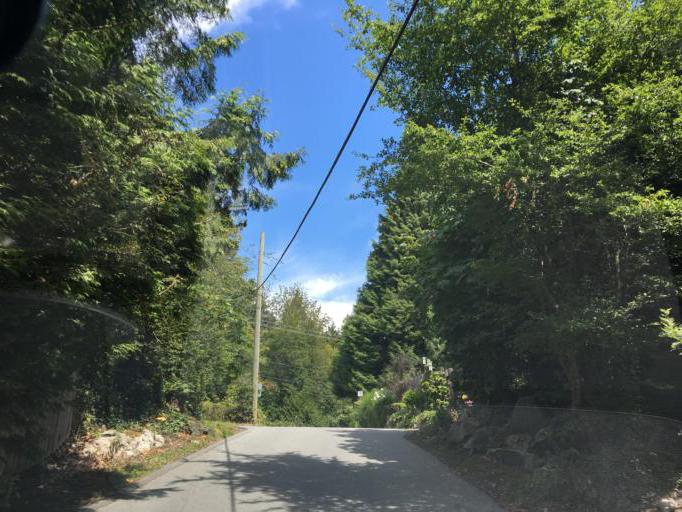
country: CA
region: British Columbia
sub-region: Greater Vancouver Regional District
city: Bowen Island
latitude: 49.3403
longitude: -123.2637
